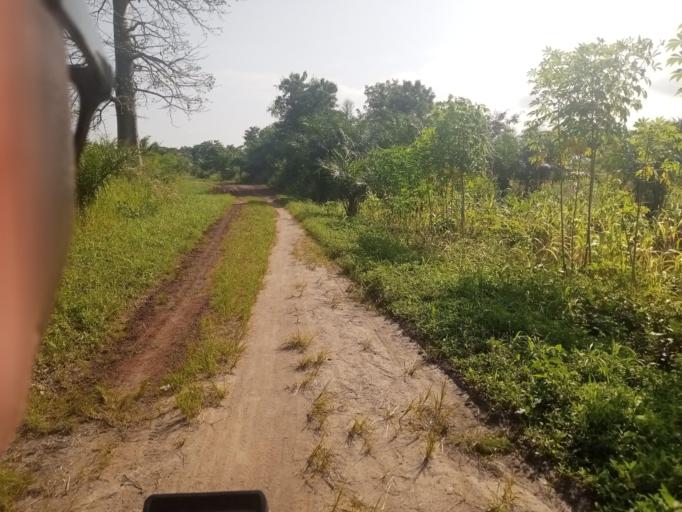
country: TG
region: Maritime
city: Tsevie
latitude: 6.6620
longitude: 0.9728
